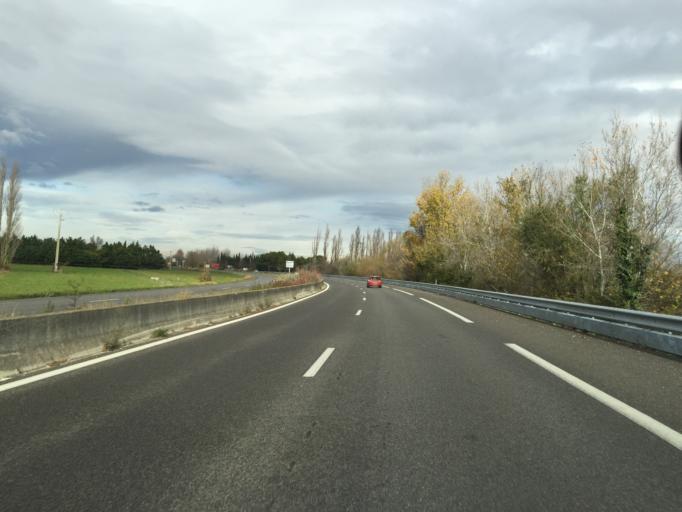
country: FR
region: Provence-Alpes-Cote d'Azur
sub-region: Departement du Vaucluse
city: Althen-des-Paluds
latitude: 43.9992
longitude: 4.9418
